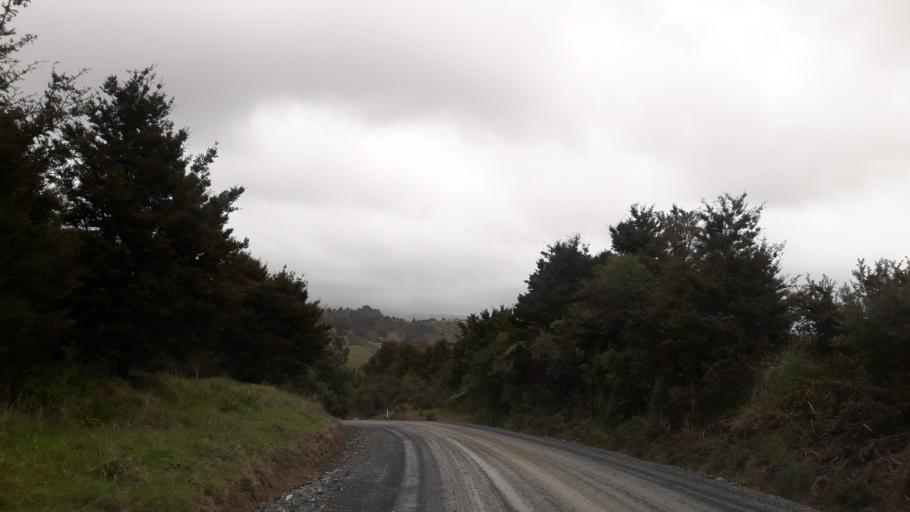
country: NZ
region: Northland
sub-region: Far North District
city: Kerikeri
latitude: -35.1275
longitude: 173.7440
